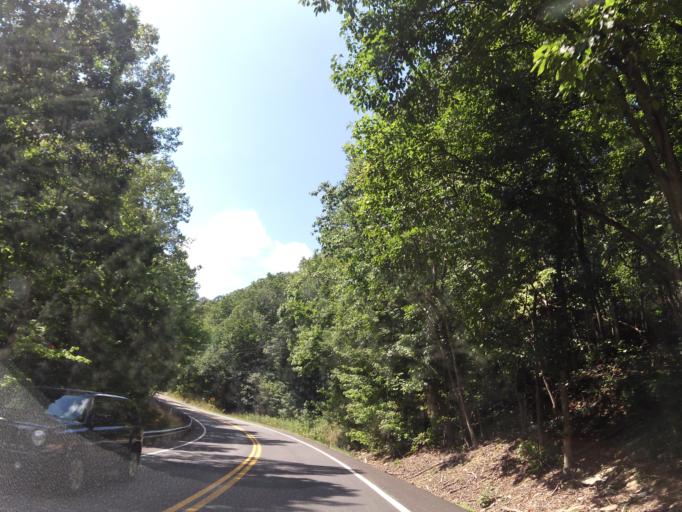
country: US
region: Tennessee
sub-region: Cumberland County
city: Fairfield Glade
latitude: 35.8821
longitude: -84.8206
